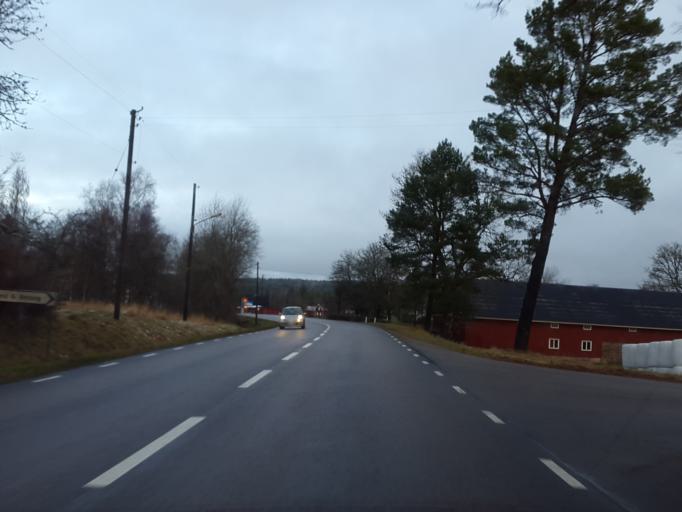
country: SE
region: Vaestra Goetaland
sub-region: Boras Kommun
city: Sandared
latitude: 57.8060
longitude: 12.7541
